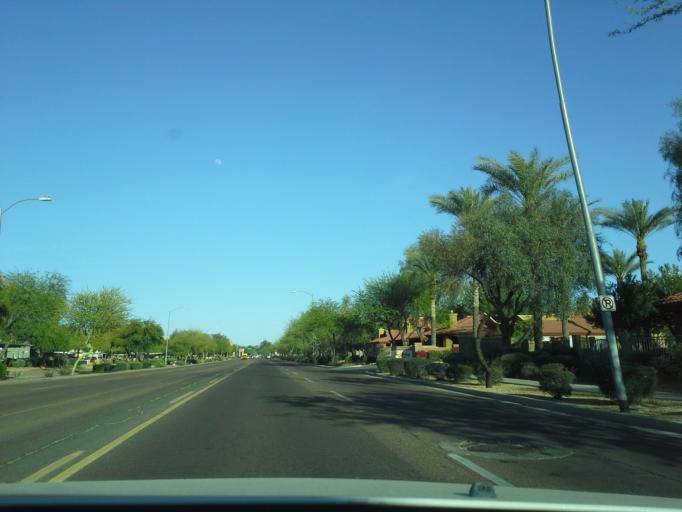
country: US
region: Arizona
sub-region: Maricopa County
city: Glendale
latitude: 33.6627
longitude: -112.1225
